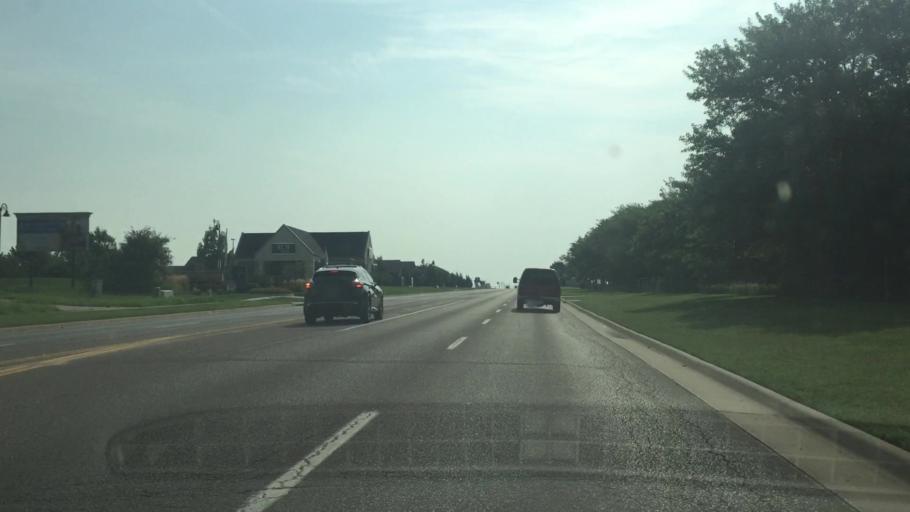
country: US
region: Kansas
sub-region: Sedgwick County
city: Bellaire
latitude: 37.7084
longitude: -97.2169
